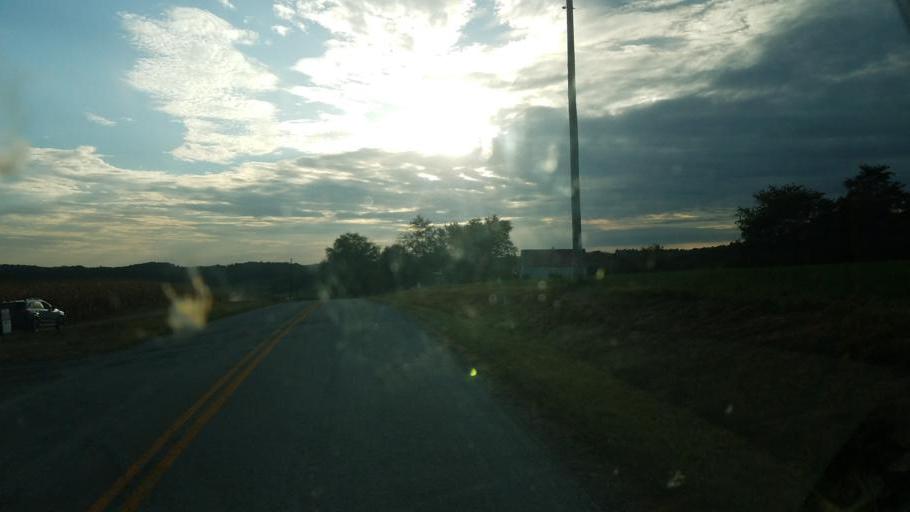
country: US
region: Ohio
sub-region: Ashland County
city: Loudonville
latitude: 40.6909
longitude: -82.2014
